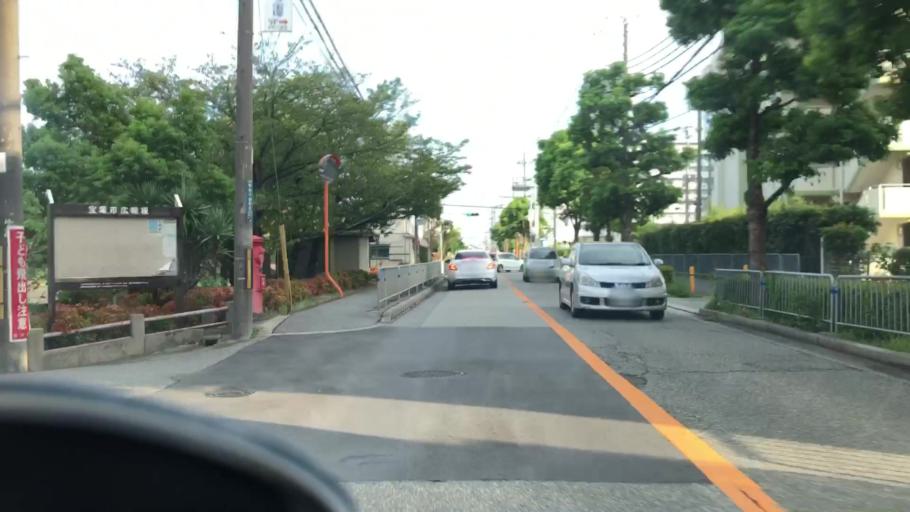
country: JP
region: Hyogo
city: Takarazuka
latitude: 34.7934
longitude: 135.3662
